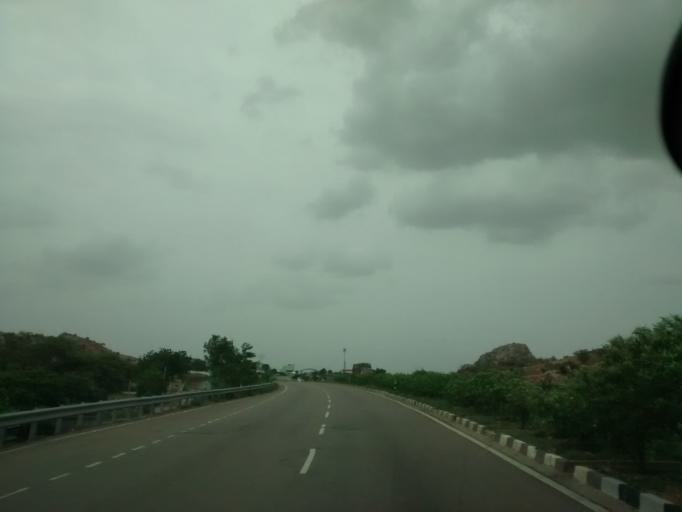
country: IN
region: Andhra Pradesh
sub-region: Kurnool
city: Ramapuram
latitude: 15.1606
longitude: 77.6732
